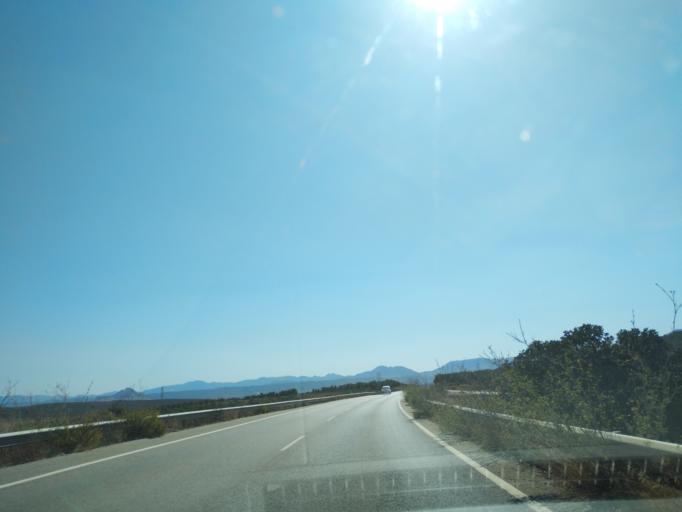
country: ES
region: Andalusia
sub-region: Provincia de Malaga
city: Mollina
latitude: 37.1092
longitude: -4.6419
